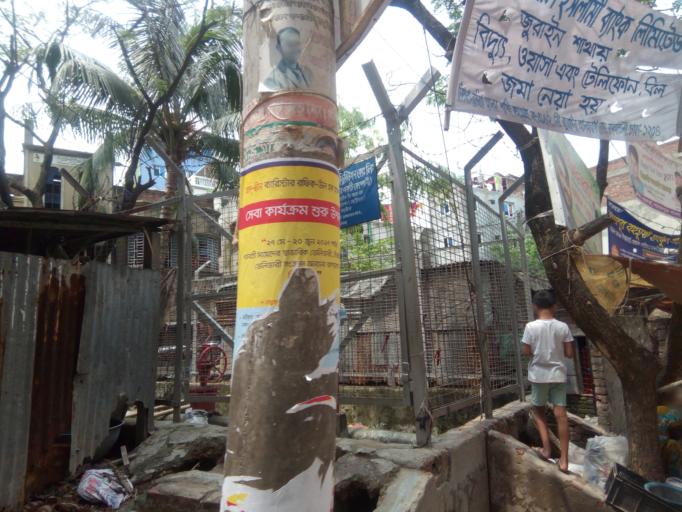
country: BD
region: Dhaka
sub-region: Dhaka
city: Dhaka
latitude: 23.6887
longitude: 90.4367
